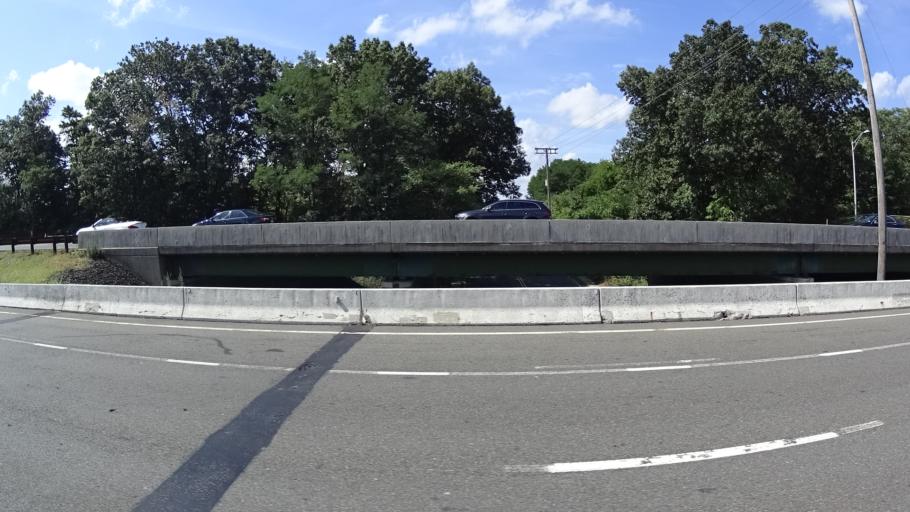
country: US
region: New Jersey
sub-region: Middlesex County
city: South Amboy
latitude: 40.4613
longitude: -74.2811
